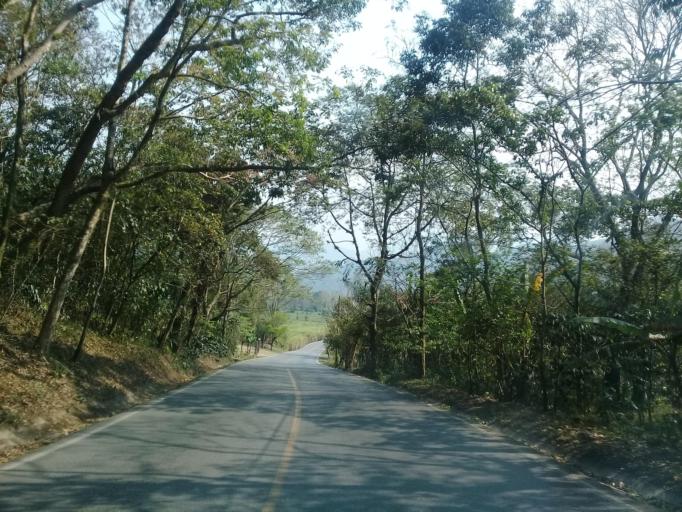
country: MX
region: Veracruz
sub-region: Ixtaczoquitlan
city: Campo Chico
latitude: 18.8389
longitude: -97.0232
